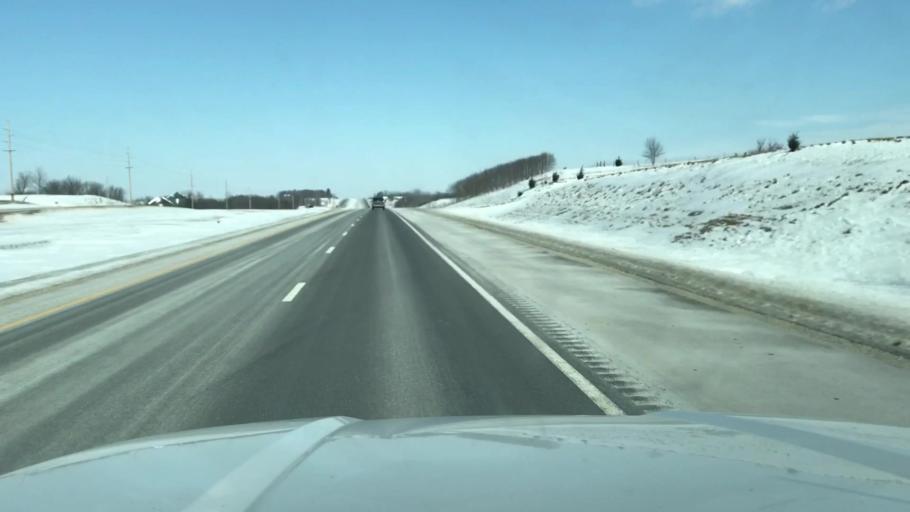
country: US
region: Missouri
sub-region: Nodaway County
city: Maryville
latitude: 40.1905
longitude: -94.8678
